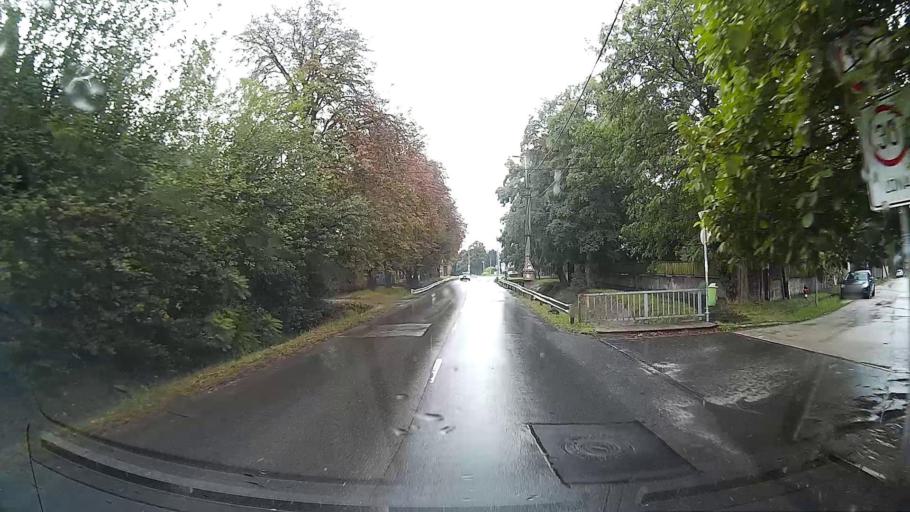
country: HU
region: Pest
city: Solymar
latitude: 47.5588
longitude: 18.9661
